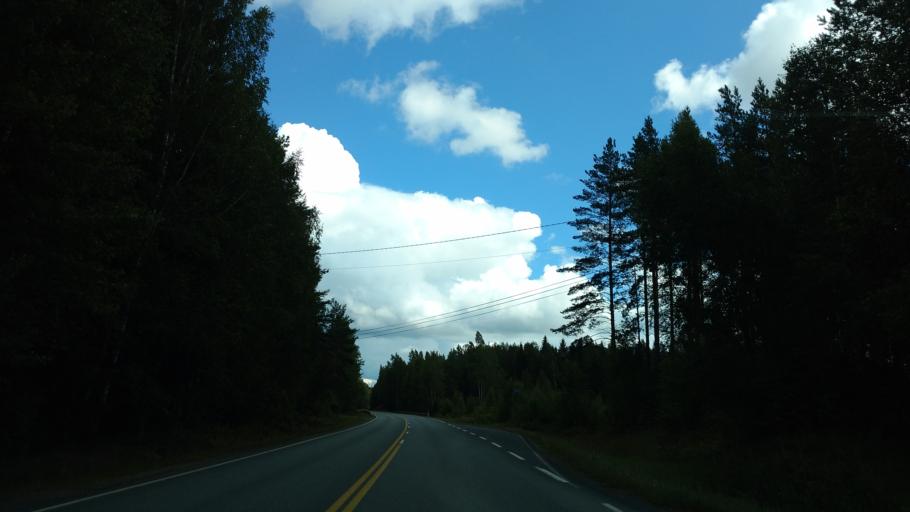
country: FI
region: Varsinais-Suomi
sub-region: Salo
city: Kisko
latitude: 60.2393
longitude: 23.5611
